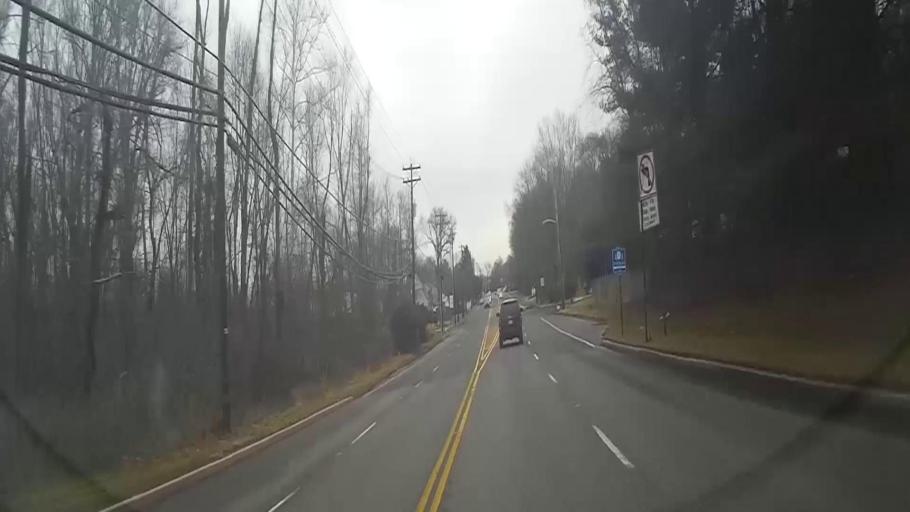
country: US
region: New Jersey
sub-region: Burlington County
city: Marlton
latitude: 39.8737
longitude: -74.9275
